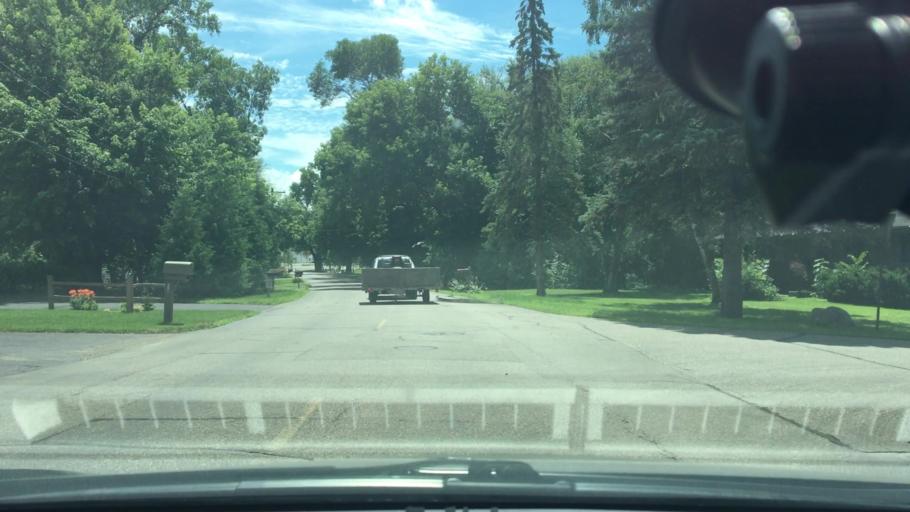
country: US
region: Minnesota
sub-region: Hennepin County
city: Plymouth
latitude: 44.9968
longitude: -93.4178
